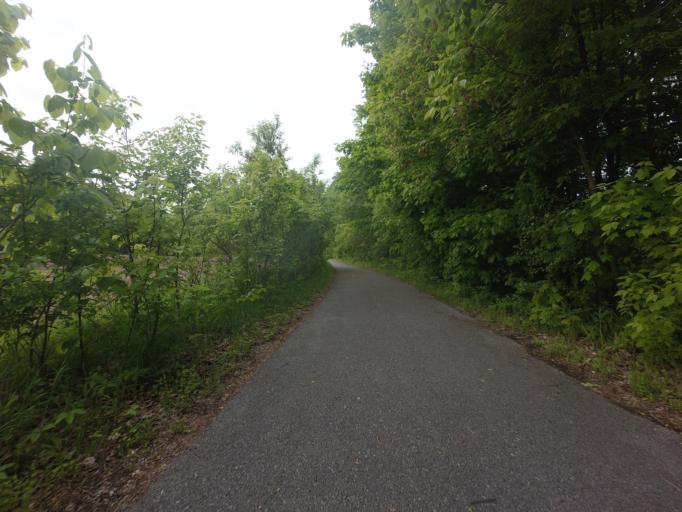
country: US
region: New York
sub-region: Jefferson County
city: Black River
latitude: 43.9950
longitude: -75.8220
